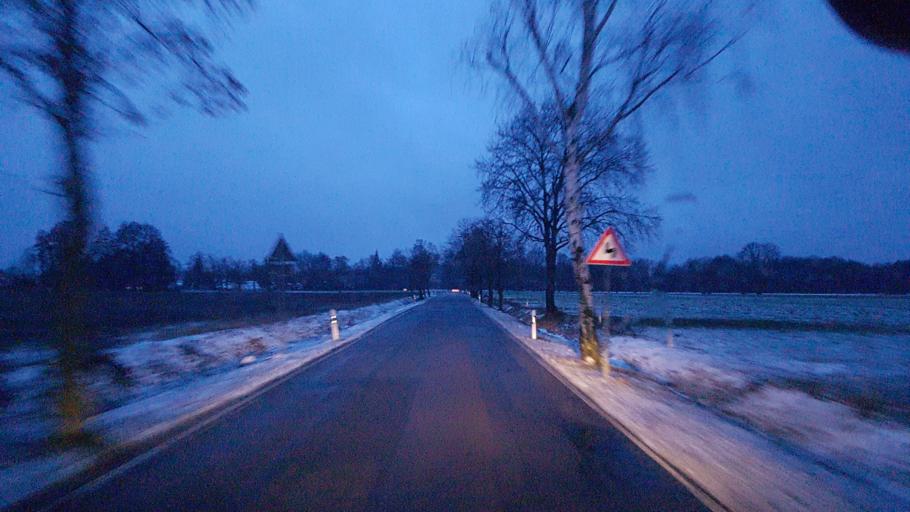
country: DE
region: Brandenburg
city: Guhrow
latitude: 51.7865
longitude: 14.2047
